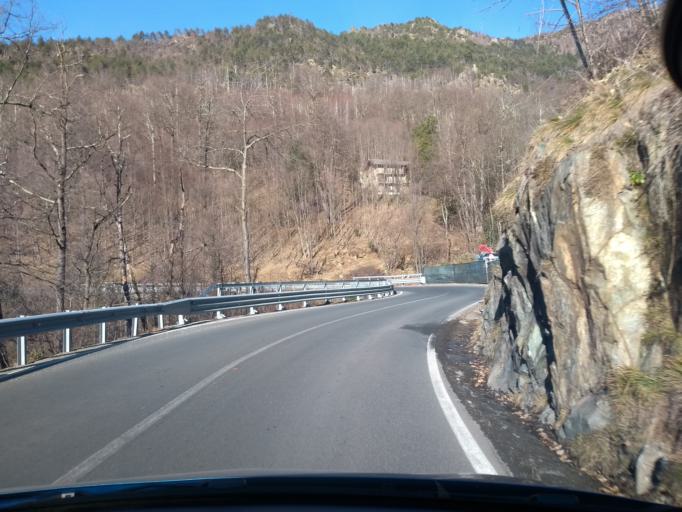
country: IT
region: Piedmont
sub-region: Provincia di Torino
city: Viu
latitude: 45.2379
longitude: 7.3993
